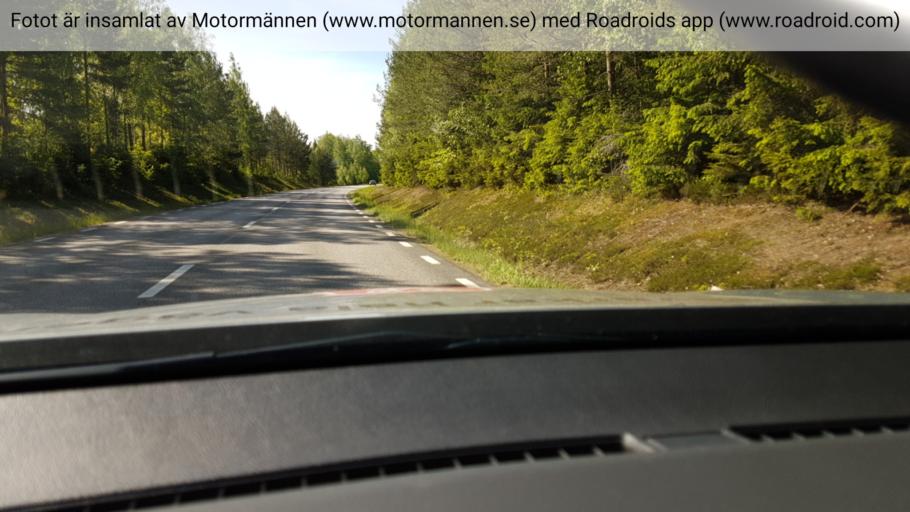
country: SE
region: Vaestra Goetaland
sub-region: Tibro Kommun
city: Tibro
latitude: 58.3843
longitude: 14.2033
